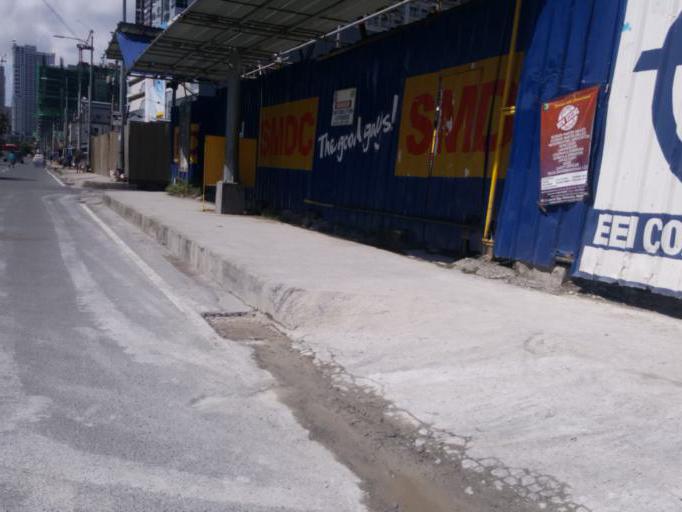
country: PH
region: Metro Manila
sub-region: City of Manila
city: Port Area
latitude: 14.5540
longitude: 120.9893
